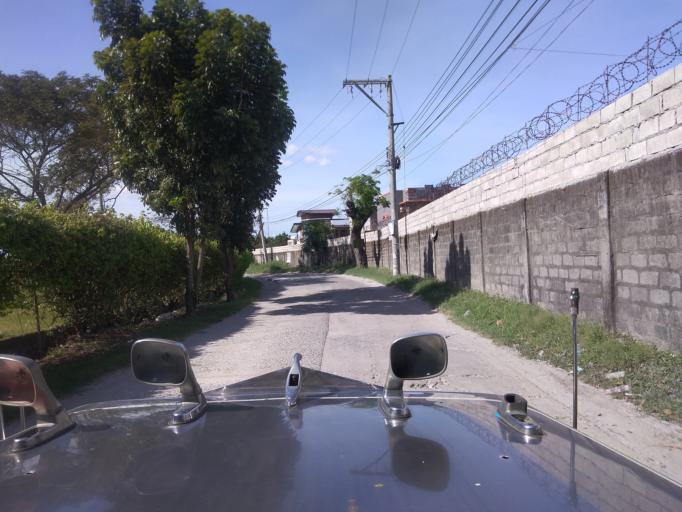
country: PH
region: Central Luzon
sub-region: Province of Pampanga
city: Magliman
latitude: 15.0401
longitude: 120.6599
